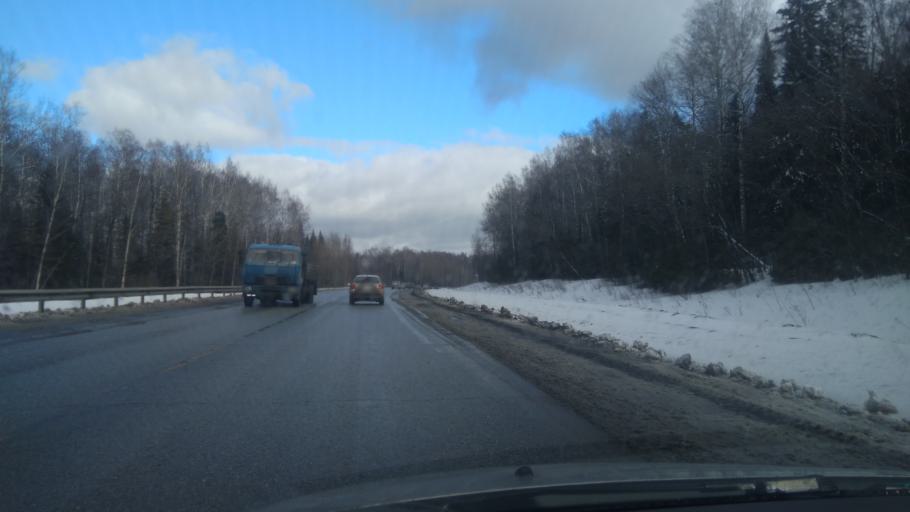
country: RU
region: Sverdlovsk
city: Bilimbay
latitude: 56.8585
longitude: 59.7167
